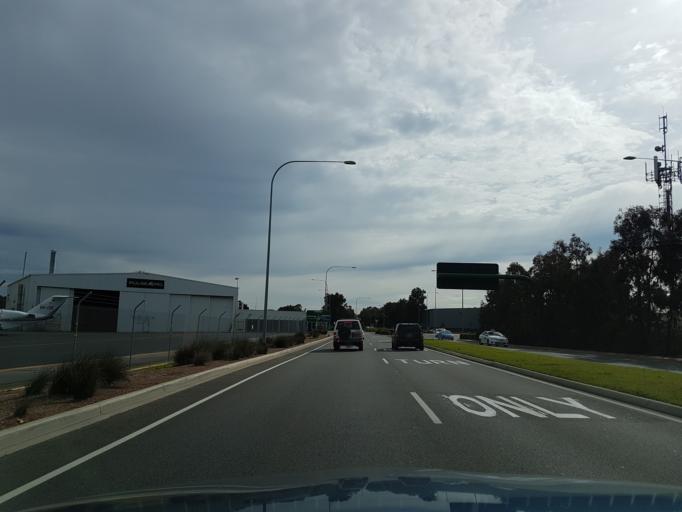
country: AU
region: South Australia
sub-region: City of West Torrens
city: Plympton
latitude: -34.9366
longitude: 138.5347
